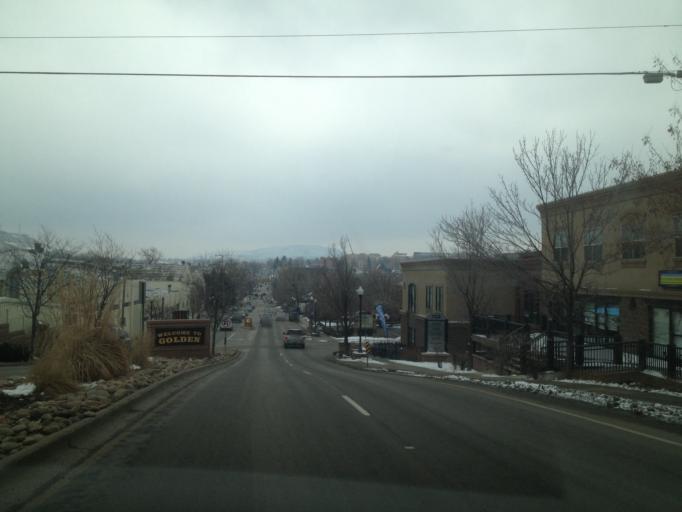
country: US
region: Colorado
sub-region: Jefferson County
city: Golden
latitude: 39.7597
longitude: -105.2254
